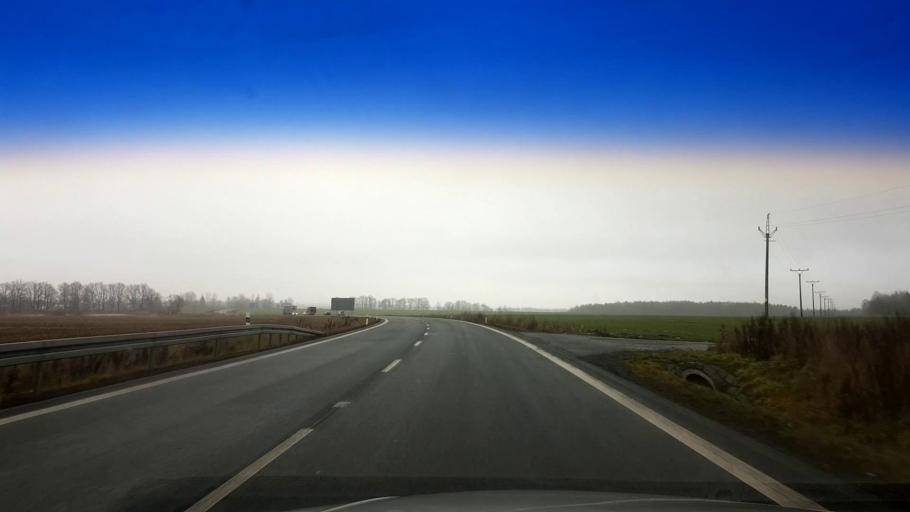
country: CZ
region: Karlovarsky
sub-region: Okres Cheb
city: Cheb
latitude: 50.0493
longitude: 12.3596
